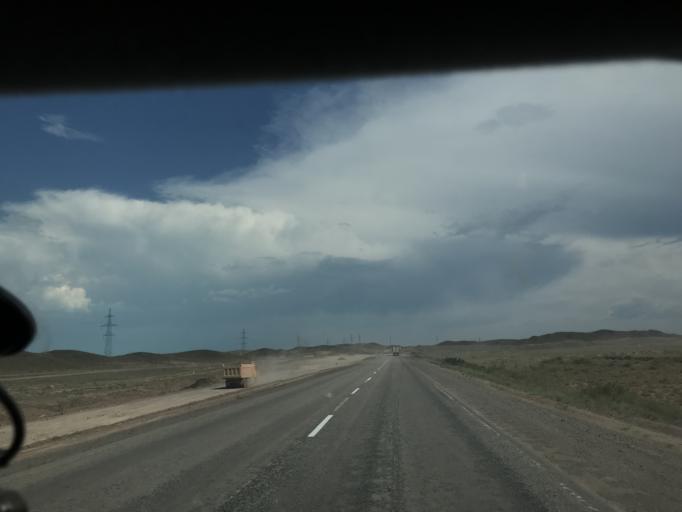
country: KZ
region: Zhambyl
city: Mynaral
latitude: 45.3635
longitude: 73.6684
